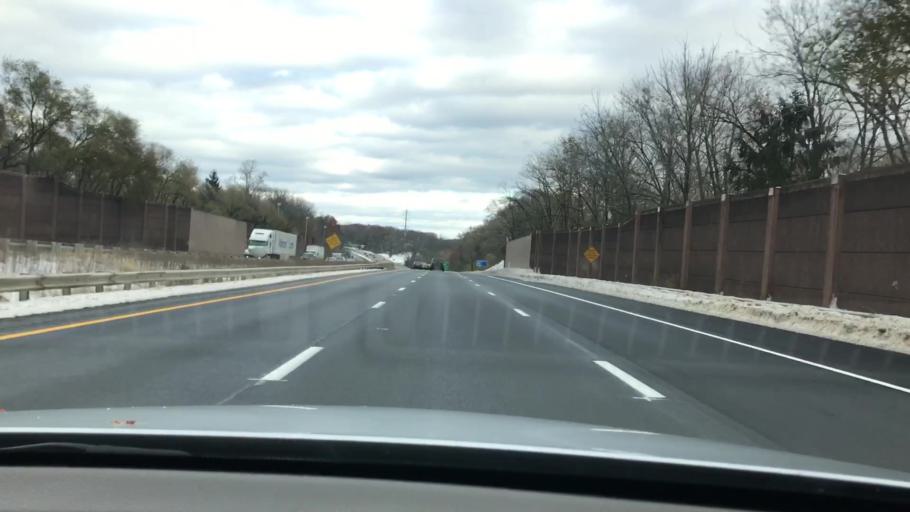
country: US
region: New Jersey
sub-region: Morris County
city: Boonton
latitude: 40.9129
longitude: -74.3780
